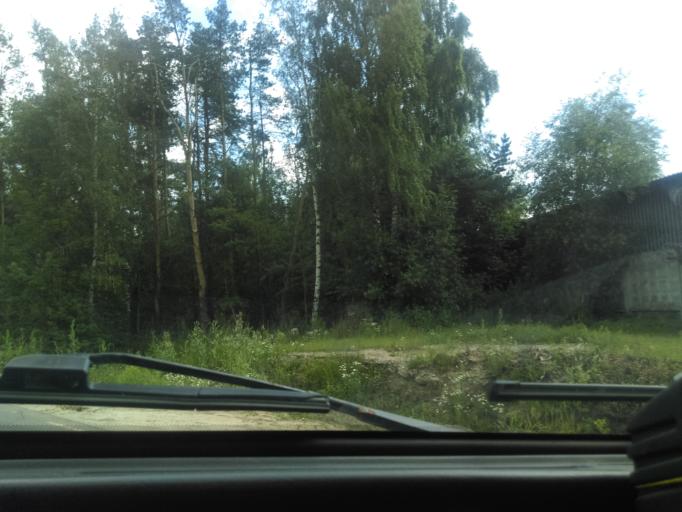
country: RU
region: Moskovskaya
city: Vostryakovo
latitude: 55.4316
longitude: 37.8730
